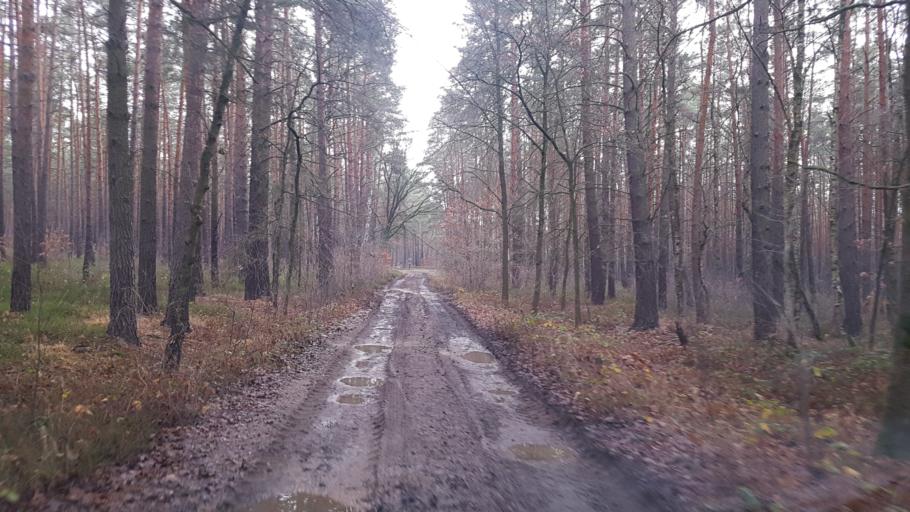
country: DE
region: Brandenburg
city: Ruckersdorf
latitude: 51.5859
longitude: 13.6205
